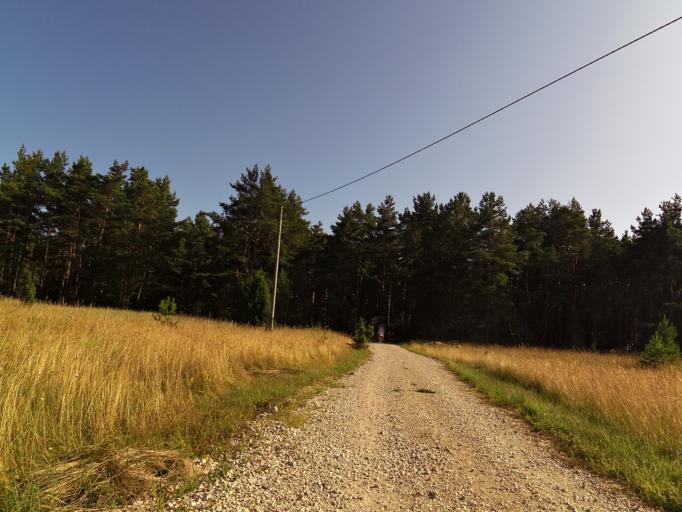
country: EE
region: Hiiumaa
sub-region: Kaerdla linn
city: Kardla
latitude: 58.8859
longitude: 22.2493
